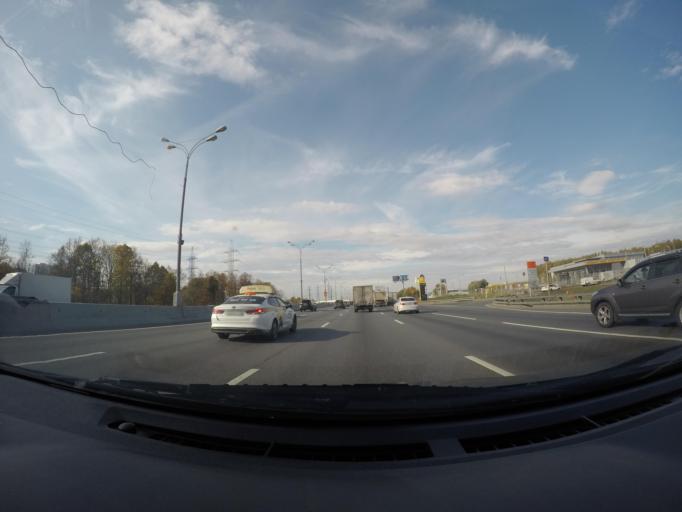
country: RU
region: Moscow
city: Lianozovo
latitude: 55.9072
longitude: 37.5984
